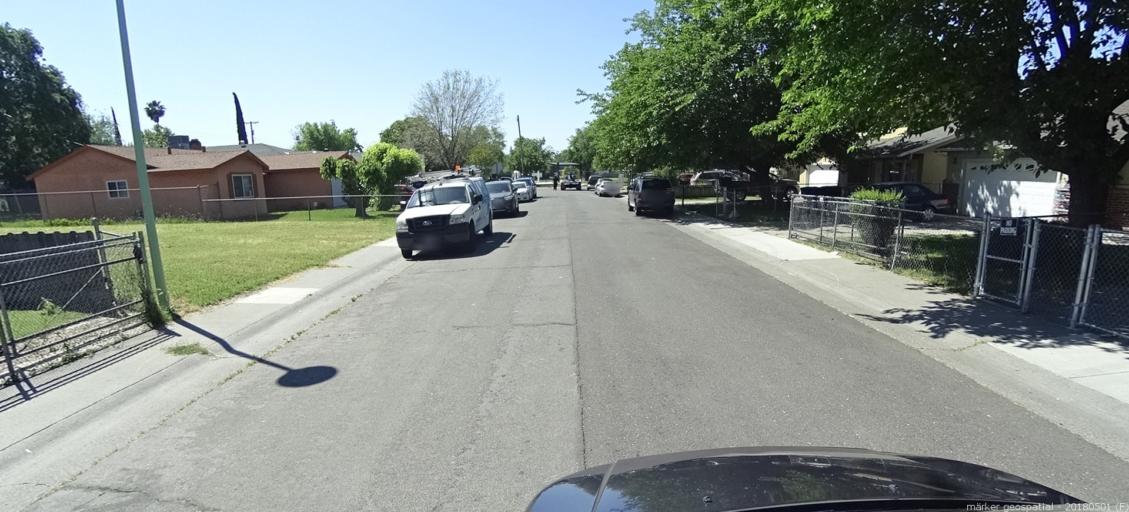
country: US
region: California
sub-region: Sacramento County
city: Rio Linda
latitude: 38.6355
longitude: -121.4406
